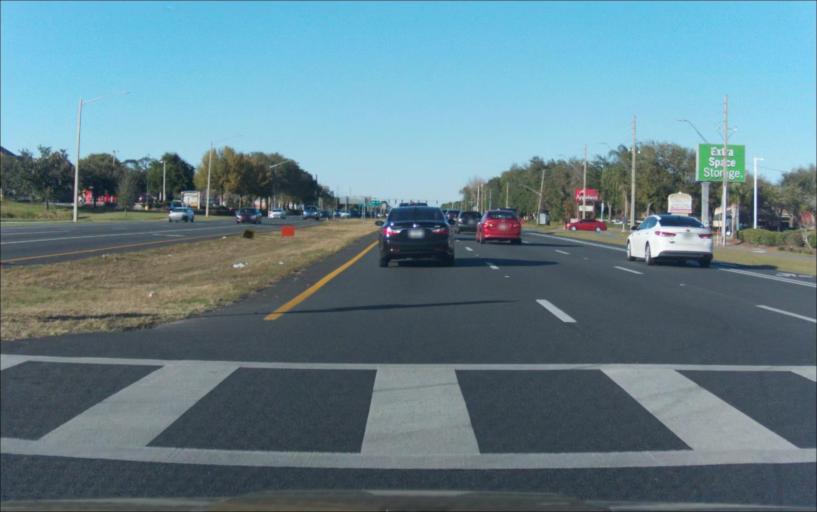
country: US
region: Florida
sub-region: Orange County
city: Orlovista
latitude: 28.5180
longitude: -81.4591
